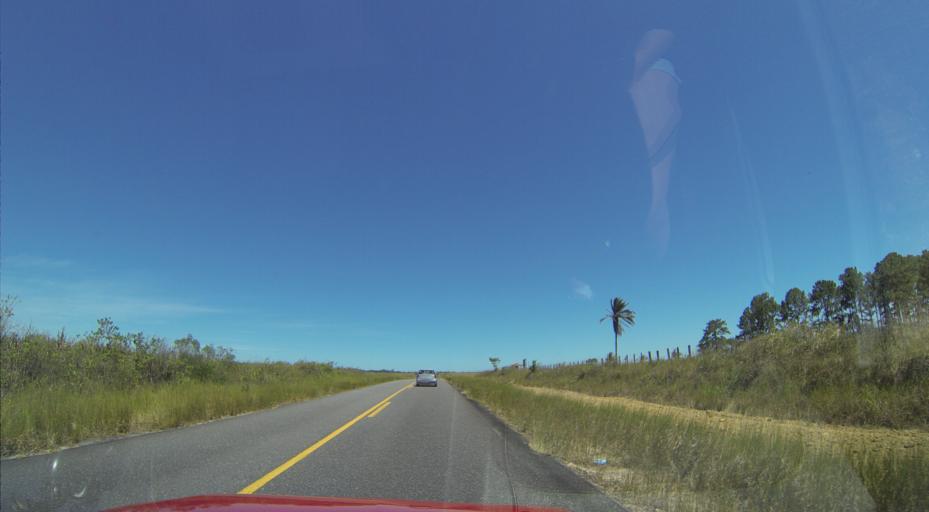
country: BR
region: Bahia
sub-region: Prado
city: Prado
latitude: -17.2323
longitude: -39.3717
